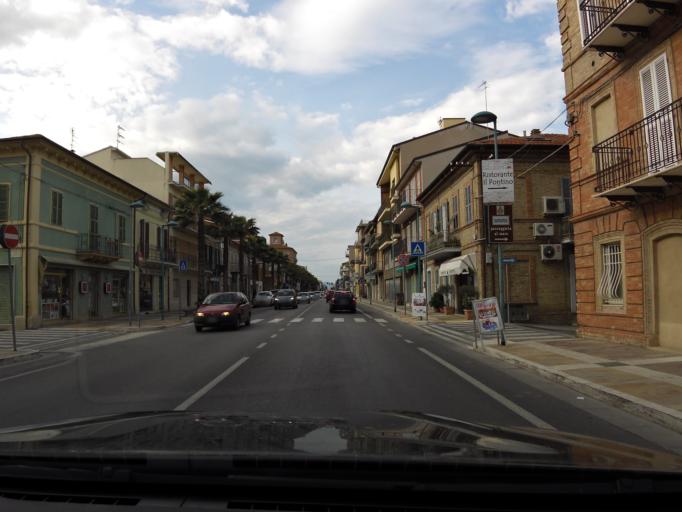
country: IT
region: The Marches
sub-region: Provincia di Macerata
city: Porto Potenza Picena
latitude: 43.3583
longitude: 13.6978
